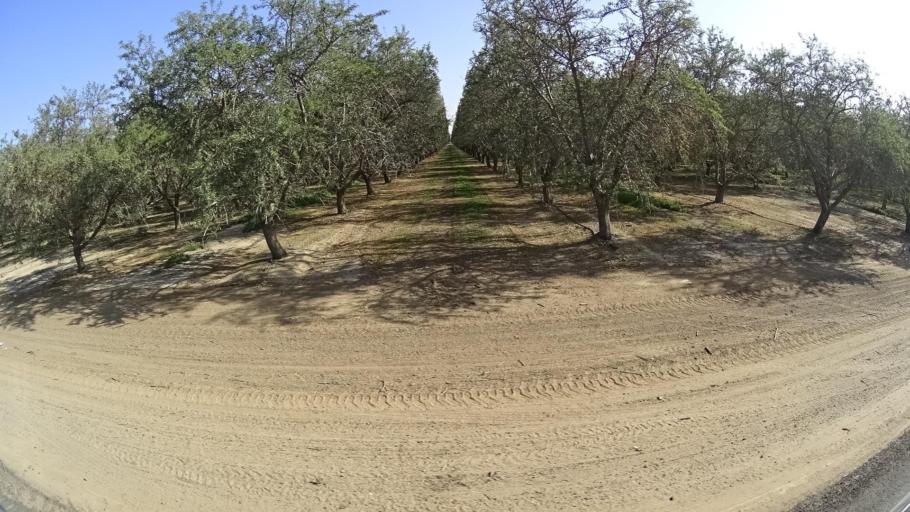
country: US
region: California
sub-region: Kern County
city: McFarland
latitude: 35.6499
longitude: -119.1867
